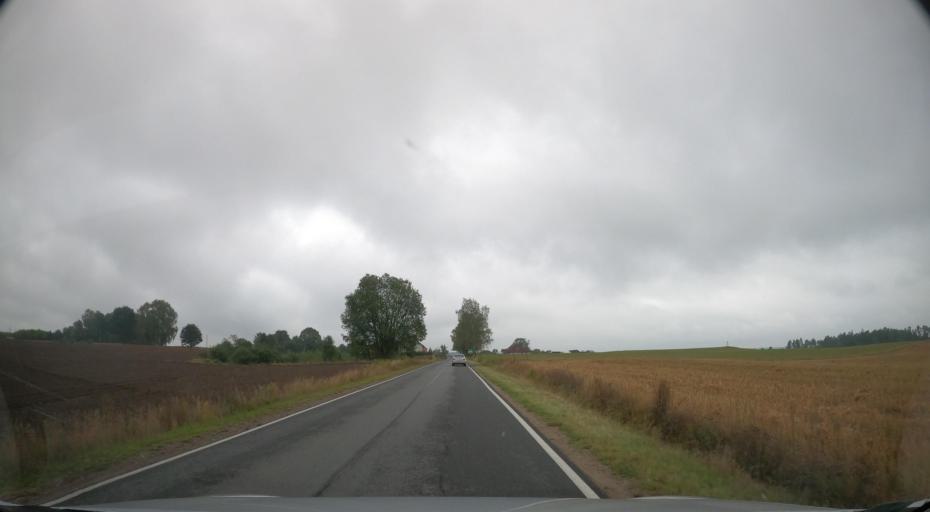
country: PL
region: Pomeranian Voivodeship
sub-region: Powiat wejherowski
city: Linia
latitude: 54.4837
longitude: 17.8493
